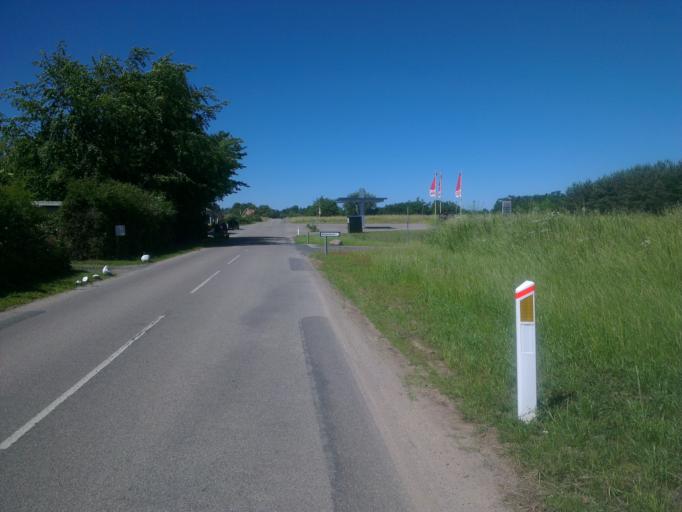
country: DK
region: Capital Region
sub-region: Frederikssund Kommune
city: Jaegerspris
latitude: 55.9105
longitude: 11.9333
